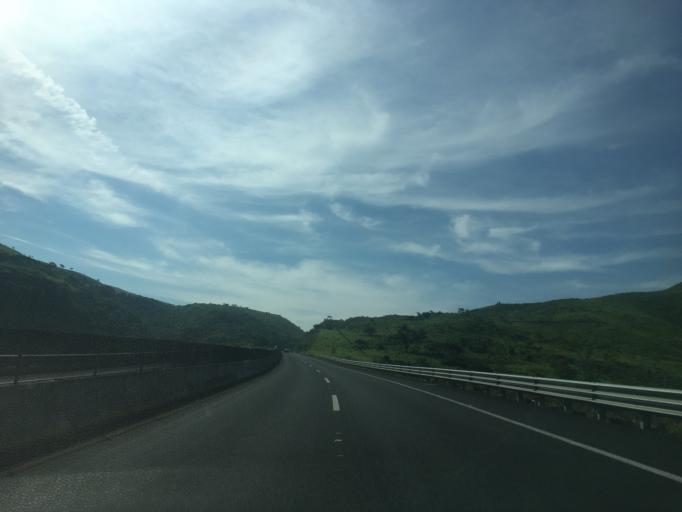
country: MX
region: Nayarit
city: Ixtlan del Rio
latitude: 21.0589
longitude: -104.4144
